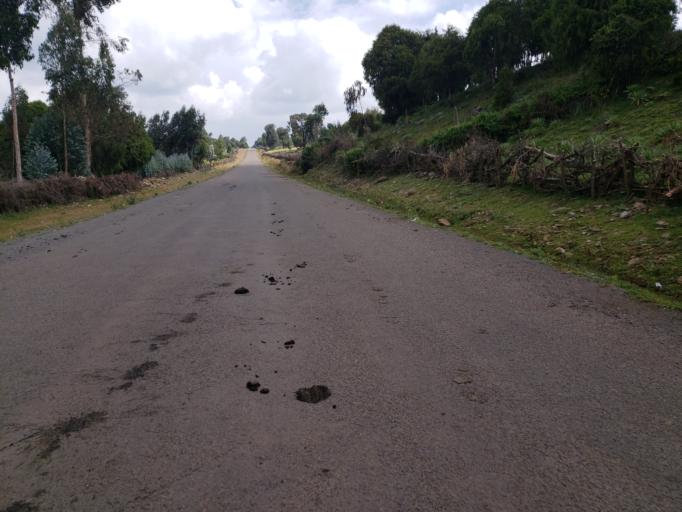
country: ET
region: Oromiya
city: Dodola
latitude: 6.8726
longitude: 39.3865
